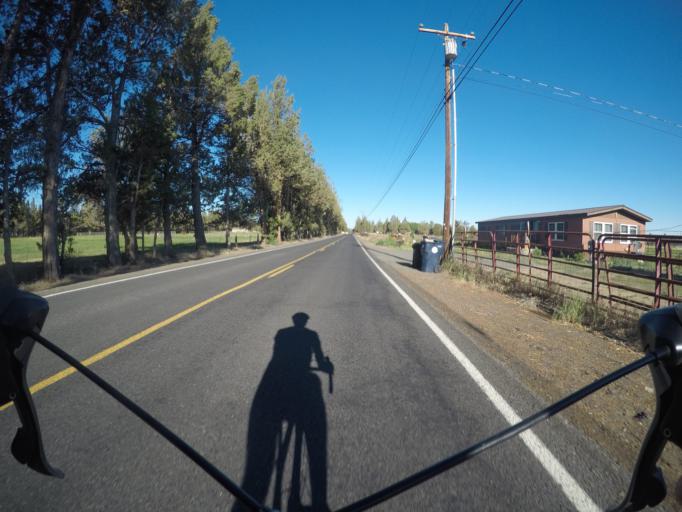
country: US
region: Oregon
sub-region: Deschutes County
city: Redmond
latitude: 44.2186
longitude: -121.2405
